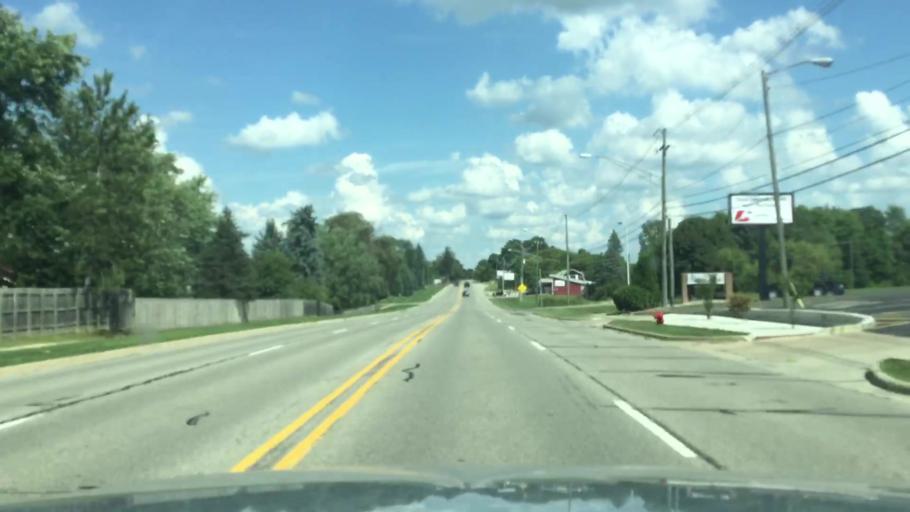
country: US
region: Michigan
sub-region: Lenawee County
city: Clinton
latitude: 42.0750
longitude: -83.9657
